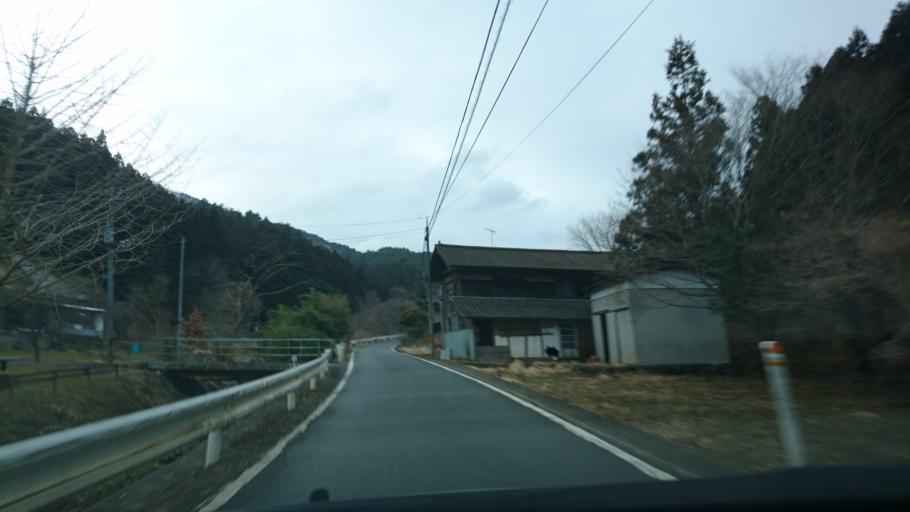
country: JP
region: Iwate
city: Ofunato
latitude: 38.9851
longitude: 141.5543
